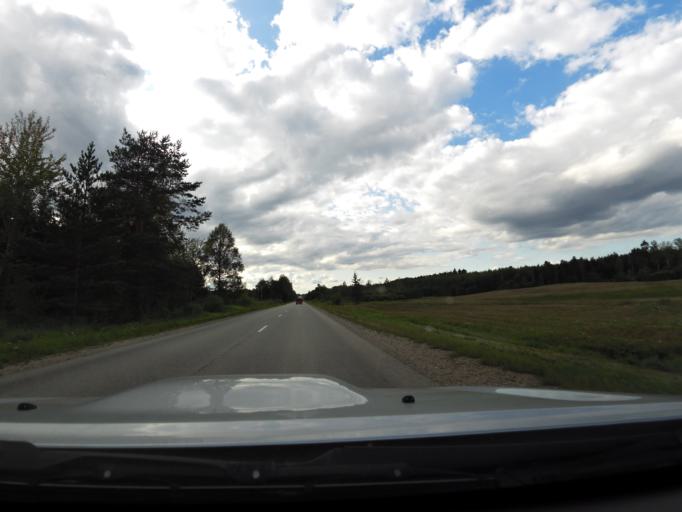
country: LV
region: Ilukste
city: Ilukste
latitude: 55.9664
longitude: 26.0407
